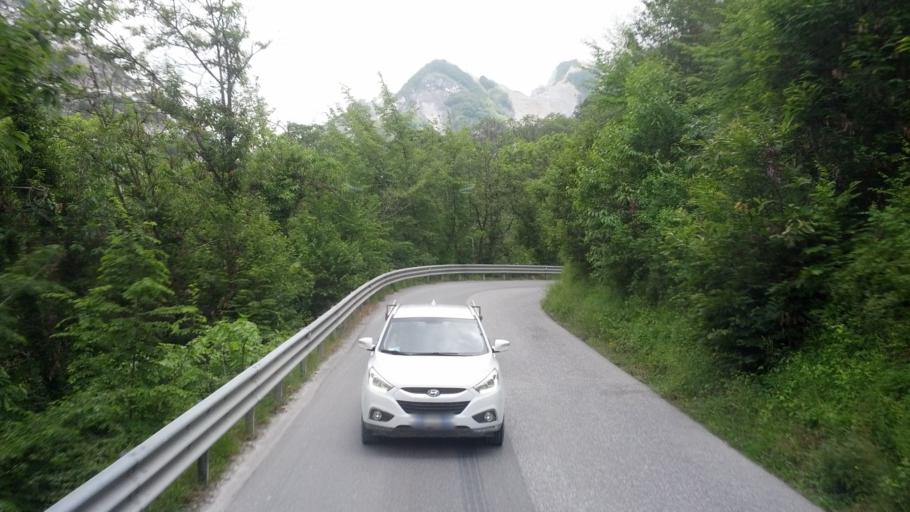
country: IT
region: Tuscany
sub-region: Provincia di Massa-Carrara
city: Massa
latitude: 44.0782
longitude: 10.1294
